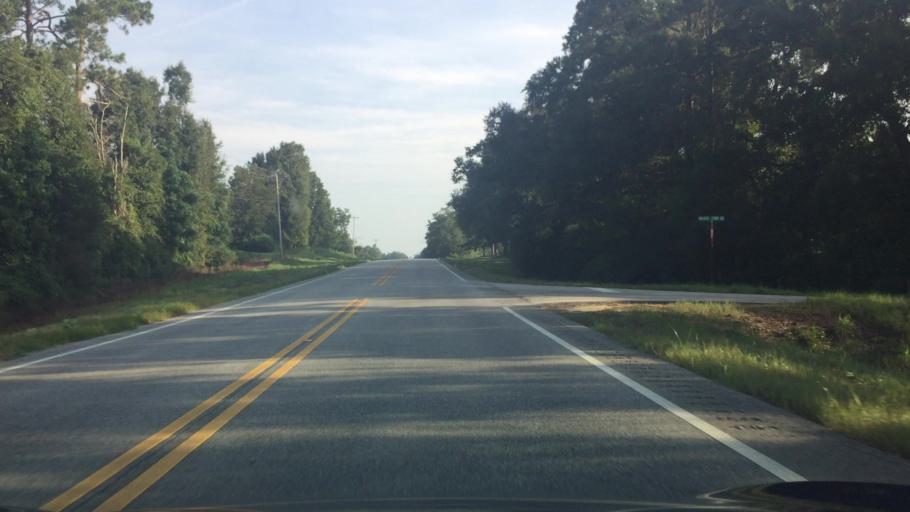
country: US
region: Alabama
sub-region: Covington County
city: Andalusia
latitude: 31.1611
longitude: -86.4590
